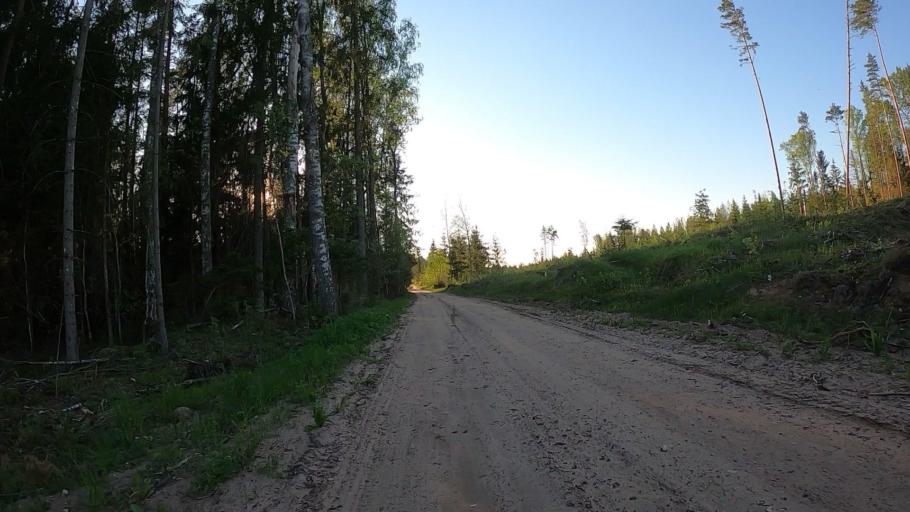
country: LV
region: Kekava
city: Kekava
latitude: 56.7760
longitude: 24.2184
